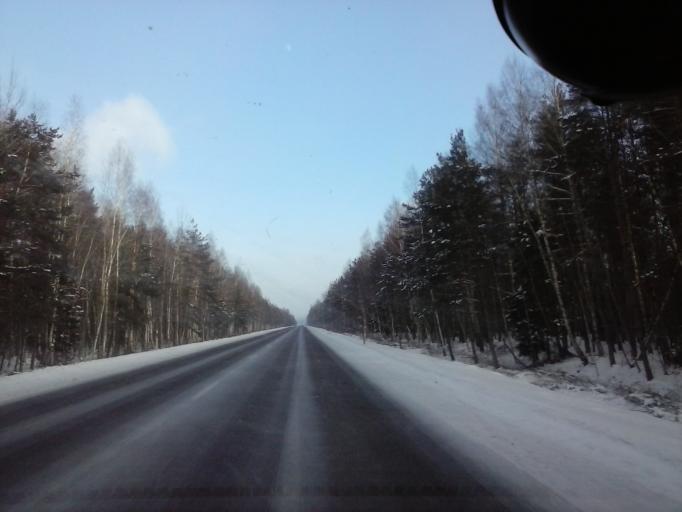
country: EE
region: Tartu
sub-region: Puhja vald
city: Puhja
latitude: 58.3272
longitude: 26.2329
